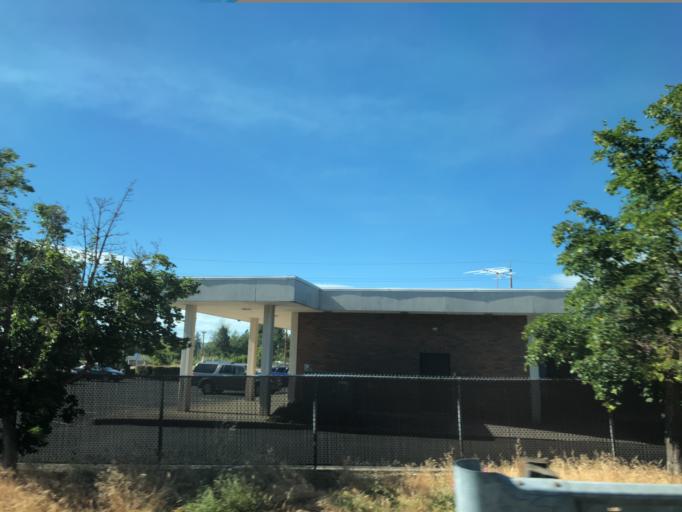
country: US
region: Oregon
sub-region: Josephine County
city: Grants Pass
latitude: 42.4218
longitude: -123.3494
